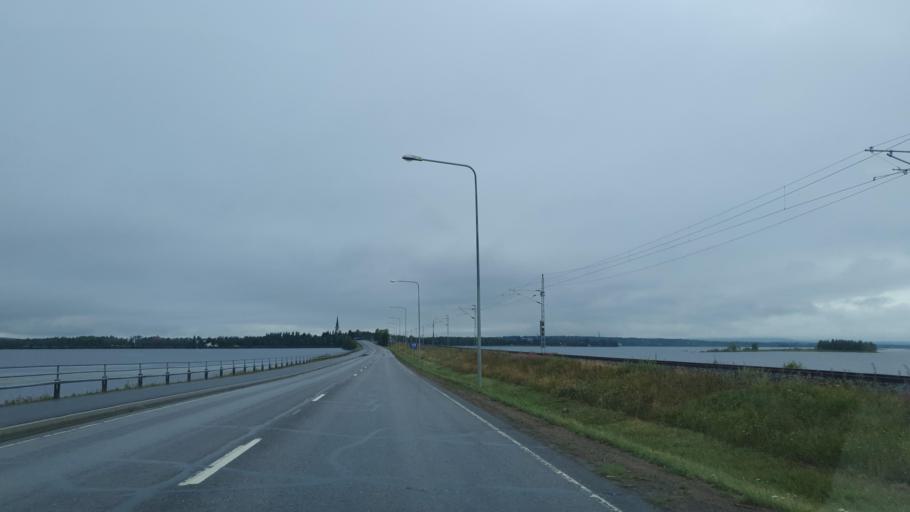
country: FI
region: Lapland
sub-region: Itae-Lappi
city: Kemijaervi
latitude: 66.7159
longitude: 27.4678
